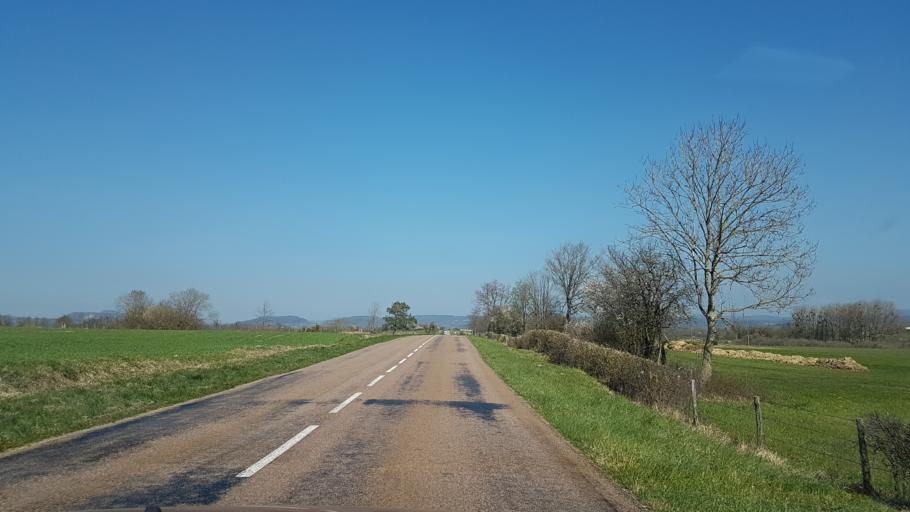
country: FR
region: Franche-Comte
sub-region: Departement du Jura
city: Clairvaux-les-Lacs
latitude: 46.5678
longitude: 5.6747
